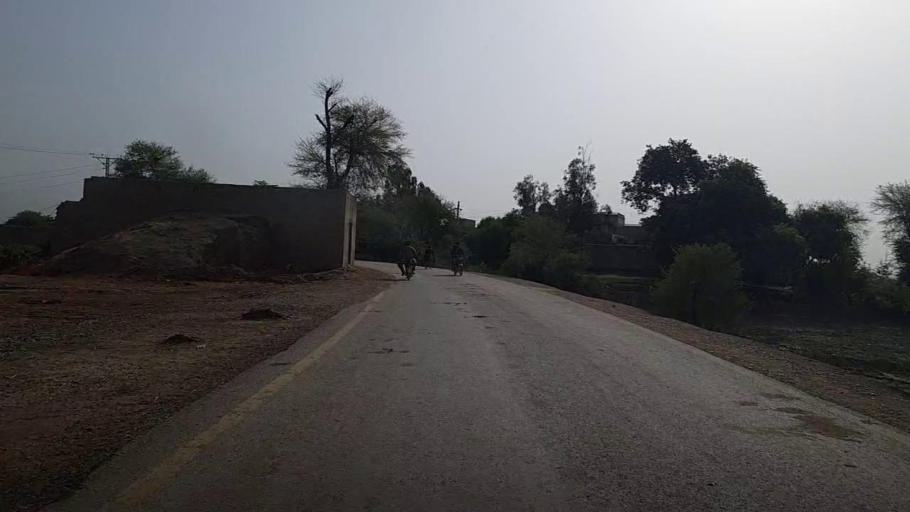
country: PK
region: Sindh
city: Khairpur Nathan Shah
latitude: 27.0937
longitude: 67.7495
